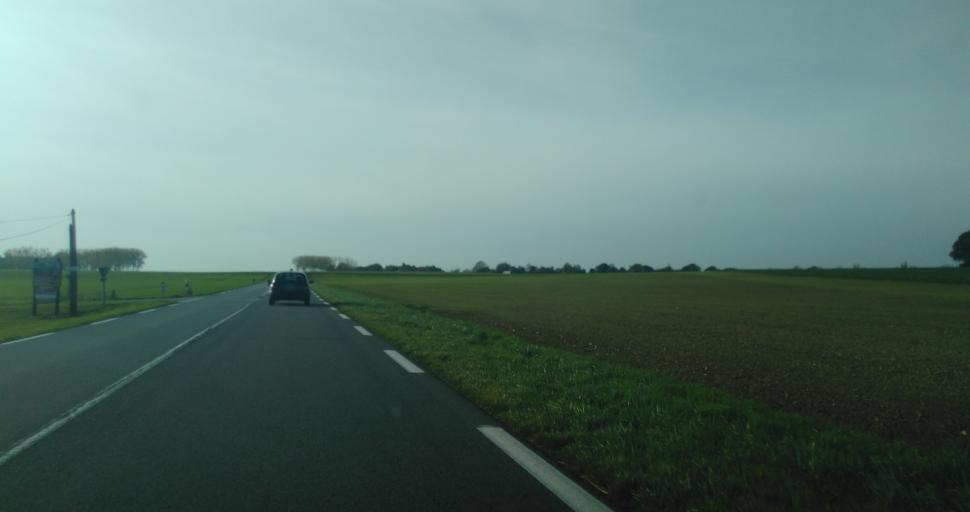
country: FR
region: Haute-Normandie
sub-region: Departement de l'Eure
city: Bourg-Achard
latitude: 49.3576
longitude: 0.7794
